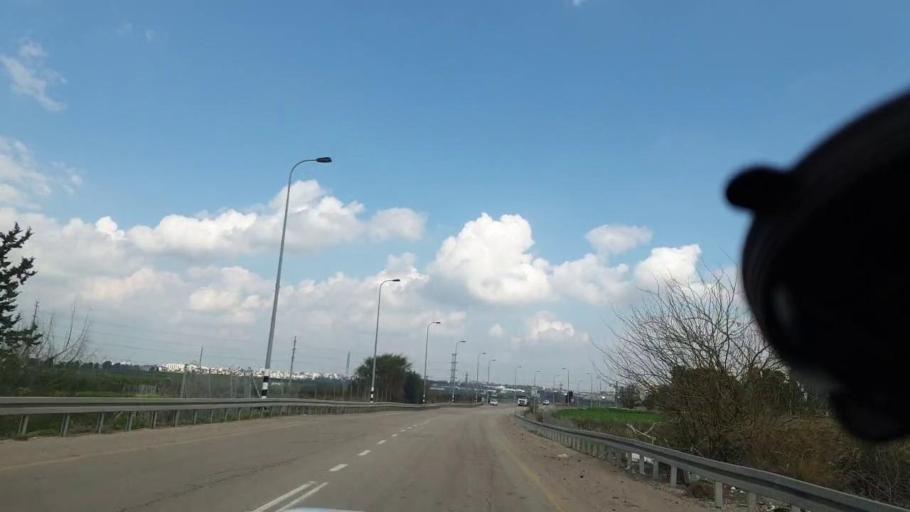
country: IL
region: Haifa
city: Ibtin
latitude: 32.7618
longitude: 35.1043
